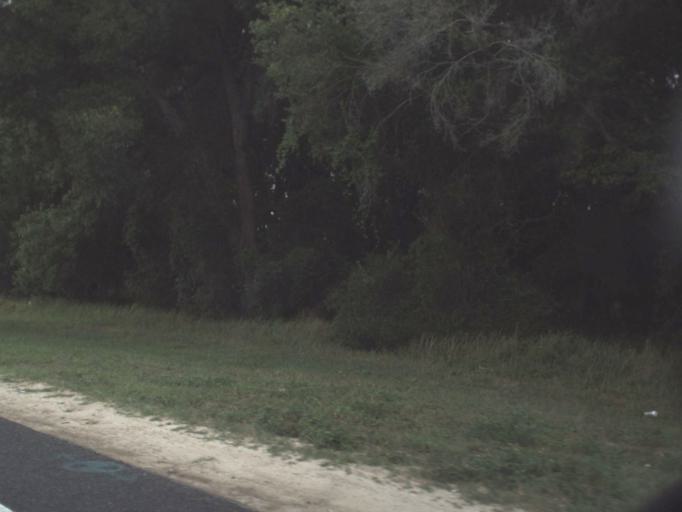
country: US
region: Florida
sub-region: Marion County
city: Belleview
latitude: 29.0088
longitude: -82.0072
